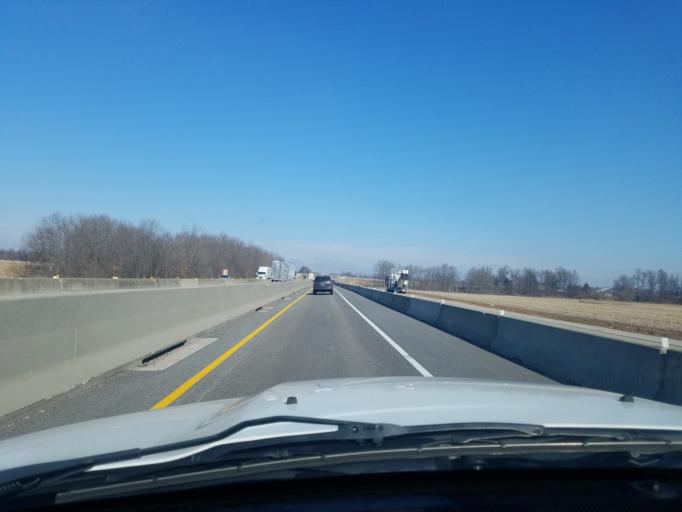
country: US
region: Kentucky
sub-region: Hardin County
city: Elizabethtown
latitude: 37.5639
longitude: -85.8756
